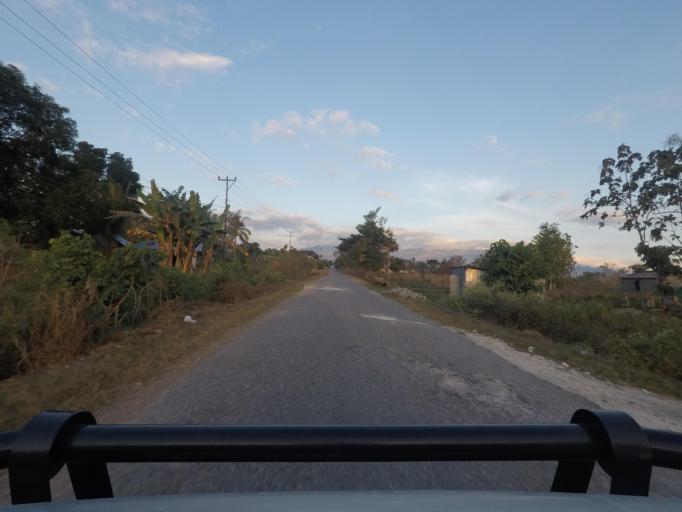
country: TL
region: Bobonaro
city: Maliana
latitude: -8.9722
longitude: 125.1344
